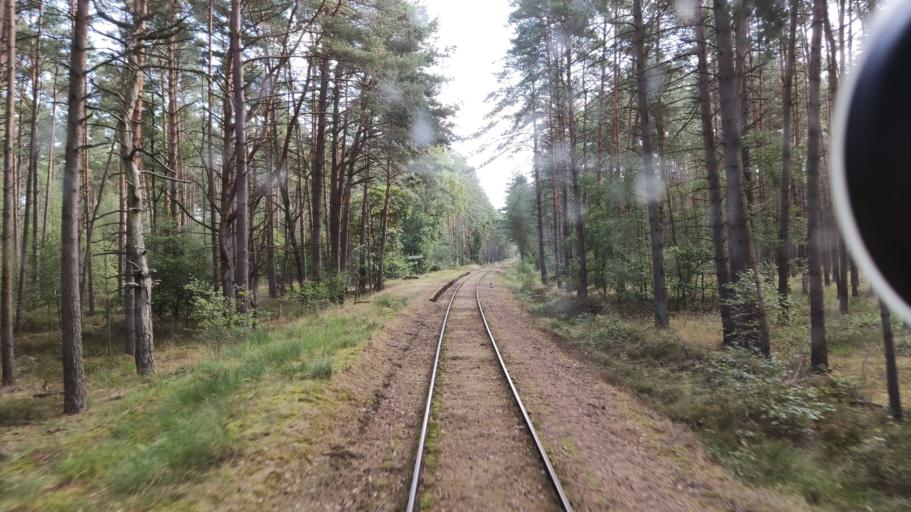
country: DE
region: Lower Saxony
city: Neetze
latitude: 53.2861
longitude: 10.6623
